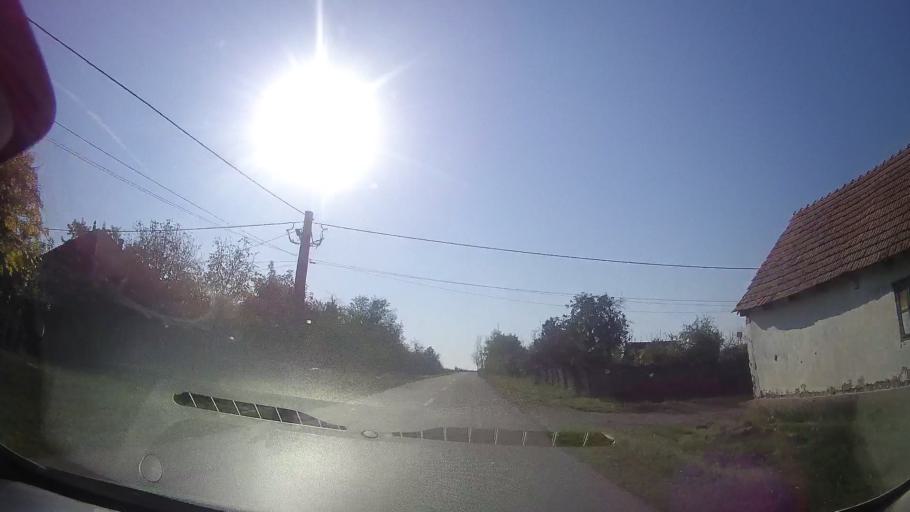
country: RO
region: Timis
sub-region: Comuna Topolovatu Mare
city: Topolovatu Mare
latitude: 45.8124
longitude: 21.5827
